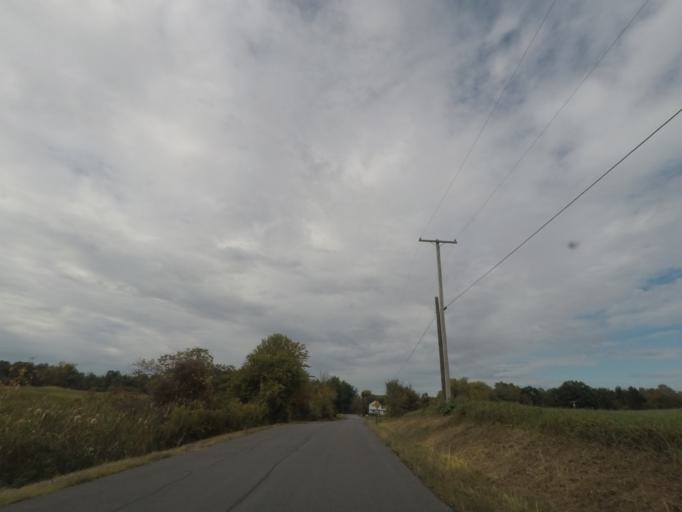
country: US
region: New York
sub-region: Rensselaer County
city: Nassau
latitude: 42.5326
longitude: -73.6441
